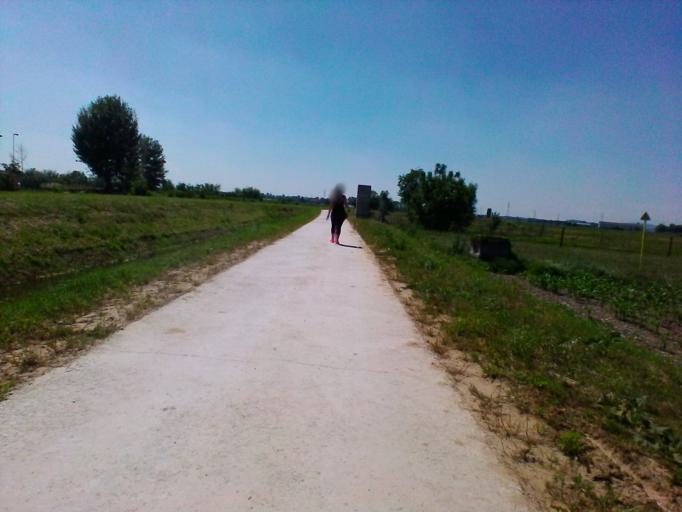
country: IT
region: Veneto
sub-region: Provincia di Verona
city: Povegliano Veronese
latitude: 45.3389
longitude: 10.8765
